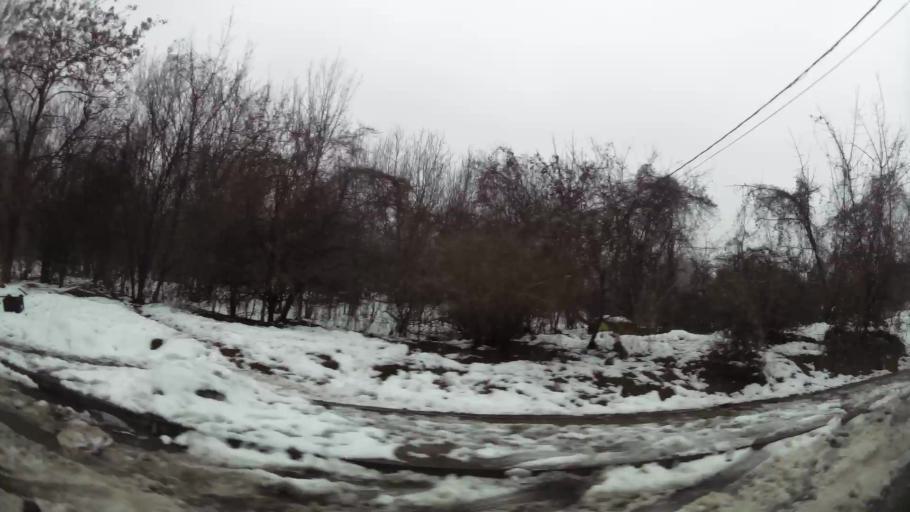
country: RS
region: Central Serbia
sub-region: Belgrade
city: Vozdovac
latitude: 44.7591
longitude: 20.4818
